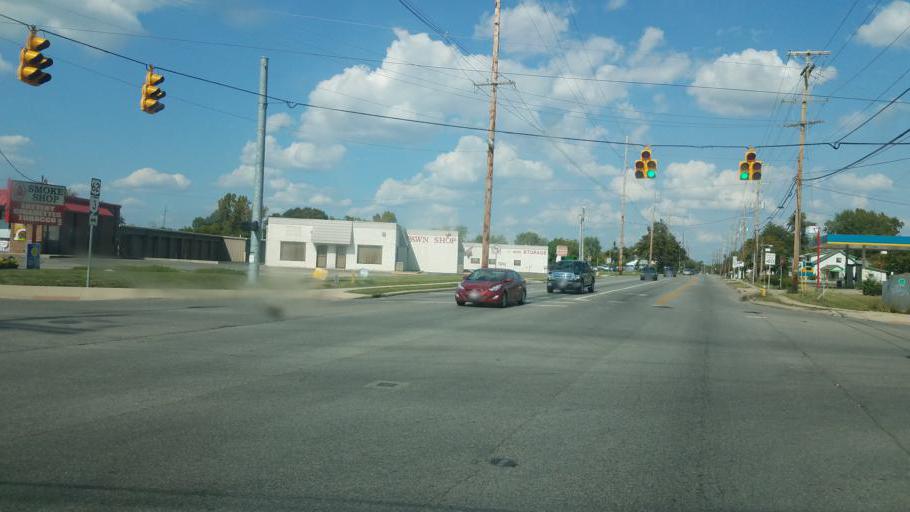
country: US
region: Ohio
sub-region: Franklin County
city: Grove City
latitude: 39.9209
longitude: -83.0615
